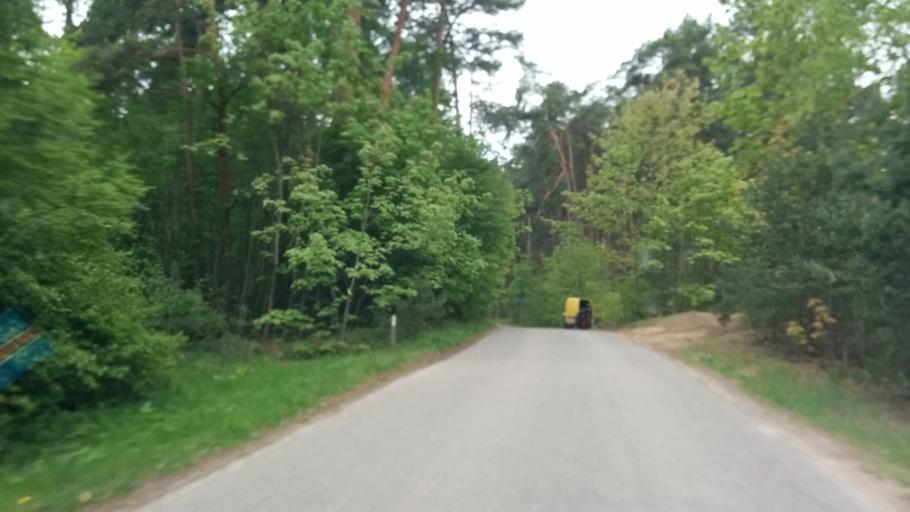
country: LV
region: Babite
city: Pinki
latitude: 56.9448
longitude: 23.9466
